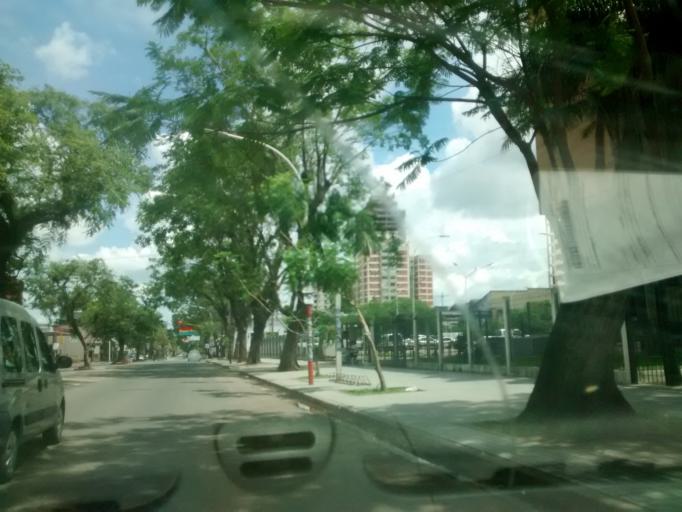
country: AR
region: Chaco
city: Resistencia
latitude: -27.4502
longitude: -58.9873
